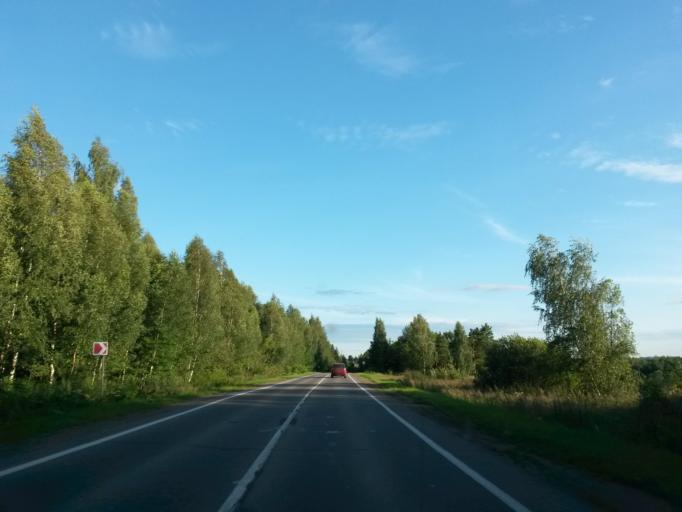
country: RU
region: Jaroslavl
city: Yaroslavl
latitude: 57.7995
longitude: 39.8273
